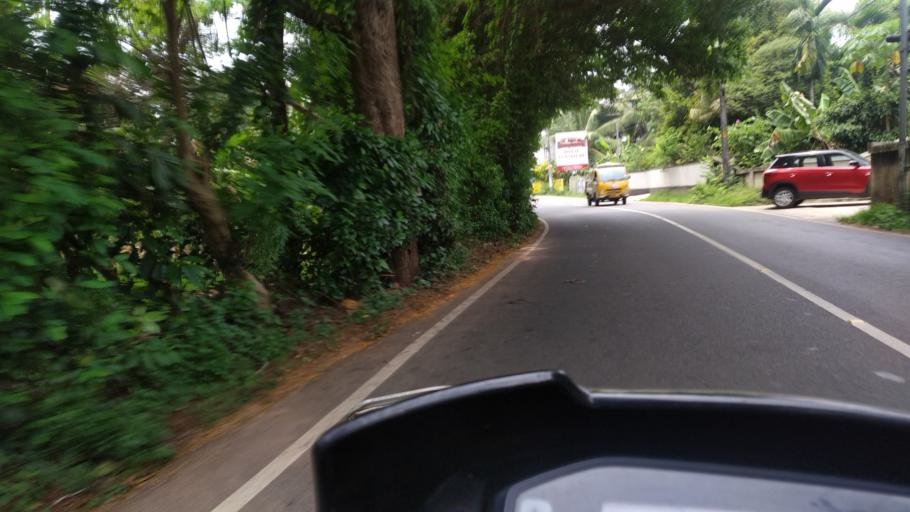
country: IN
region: Kerala
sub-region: Ernakulam
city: Aluva
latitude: 10.1559
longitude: 76.3170
